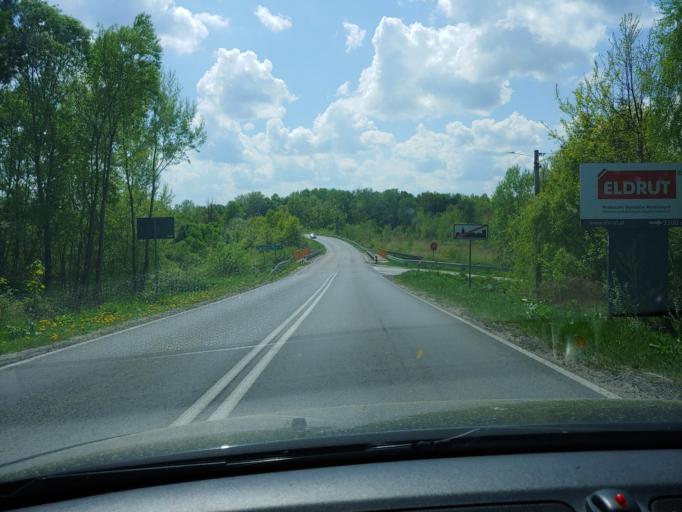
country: PL
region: Subcarpathian Voivodeship
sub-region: Powiat mielecki
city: Wadowice Gorne
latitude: 50.2391
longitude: 21.2851
